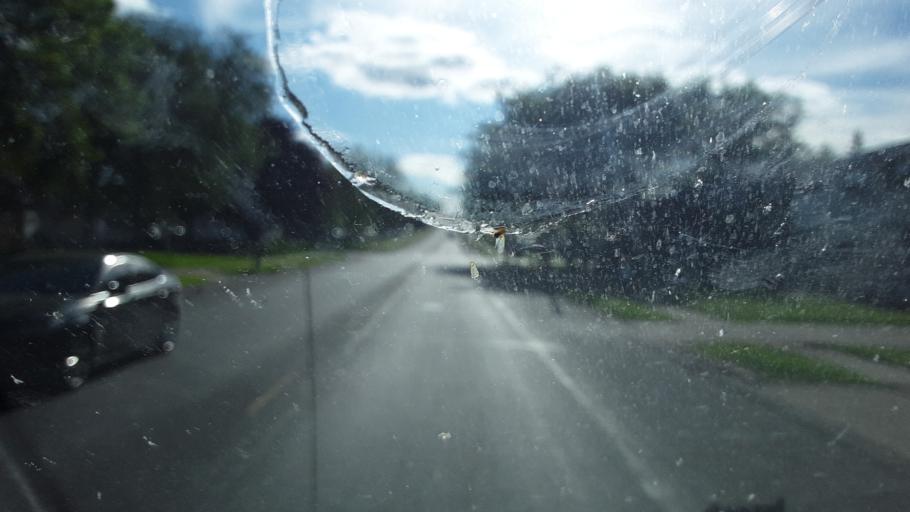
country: US
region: Wisconsin
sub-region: Wood County
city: Marshfield
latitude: 44.6556
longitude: -90.1889
